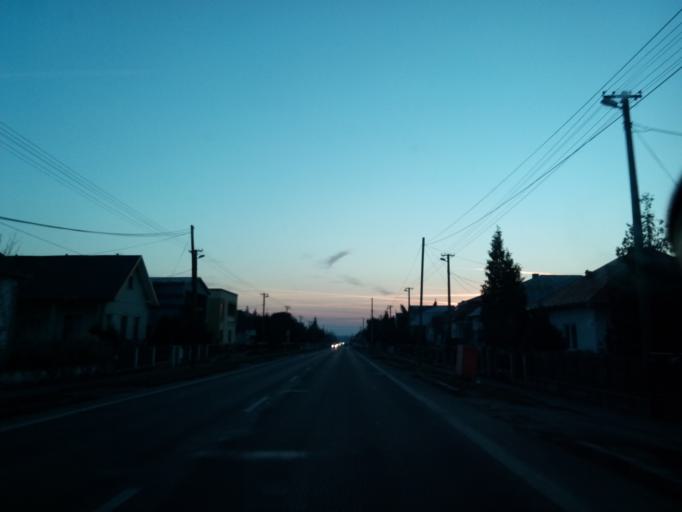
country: SK
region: Kosicky
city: Vinne
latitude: 48.7602
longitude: 21.9899
